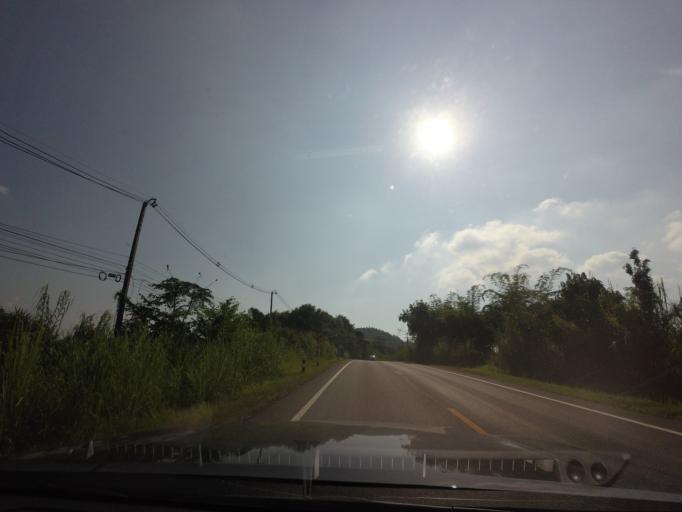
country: TH
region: Nan
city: Santi Suk
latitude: 18.9203
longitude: 100.8907
